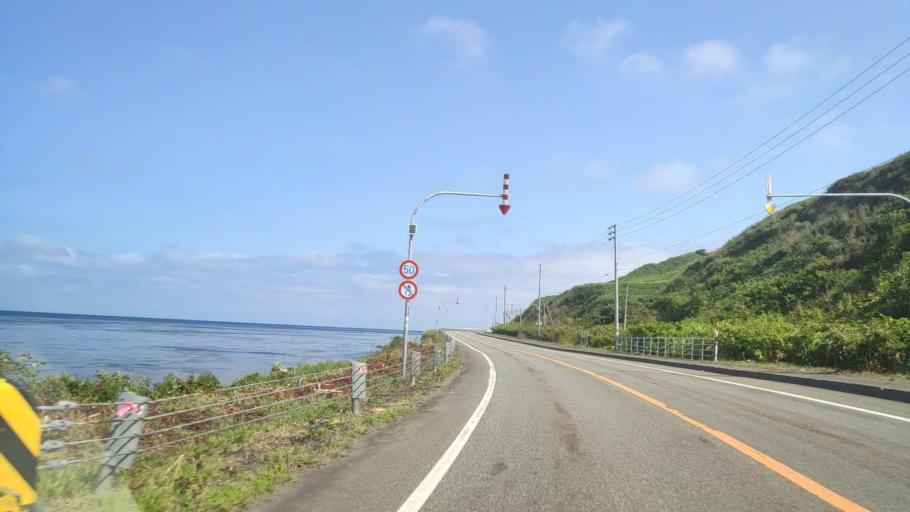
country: JP
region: Hokkaido
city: Makubetsu
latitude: 45.5031
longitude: 141.8930
